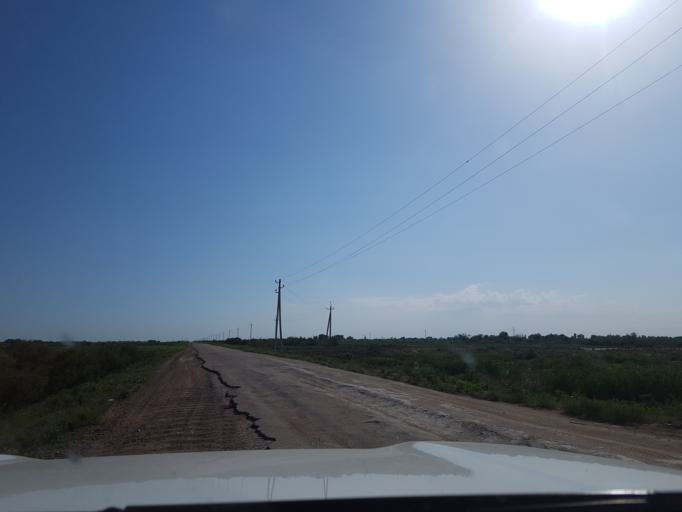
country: TM
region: Dasoguz
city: Koeneuergench
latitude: 42.0550
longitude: 58.8369
